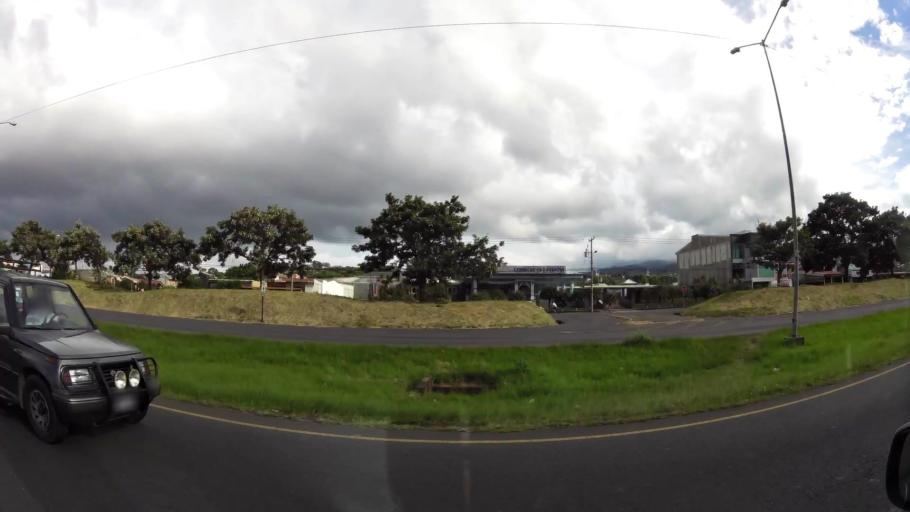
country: CR
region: Cartago
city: San Diego
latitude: 9.9007
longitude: -84.0041
